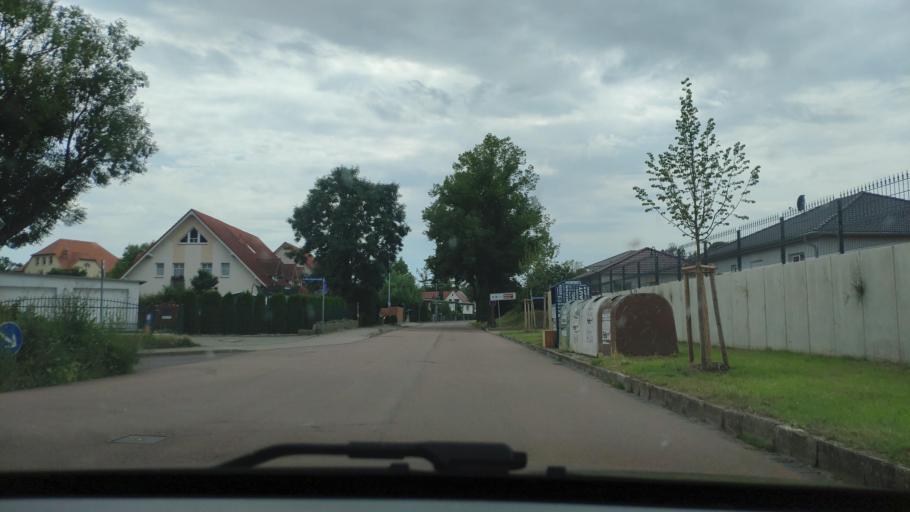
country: DE
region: Saxony-Anhalt
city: Bernburg
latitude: 51.7994
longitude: 11.7245
